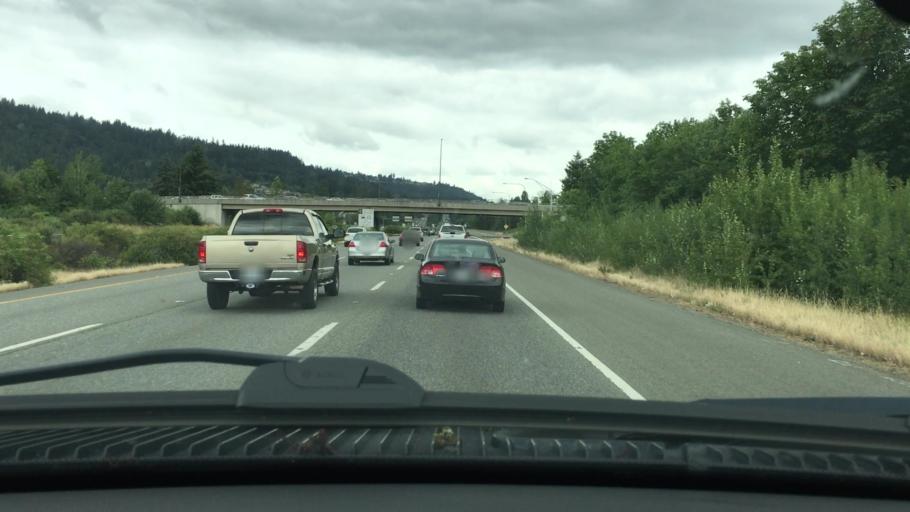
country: US
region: Washington
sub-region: King County
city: Issaquah
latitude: 47.5479
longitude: -122.0588
